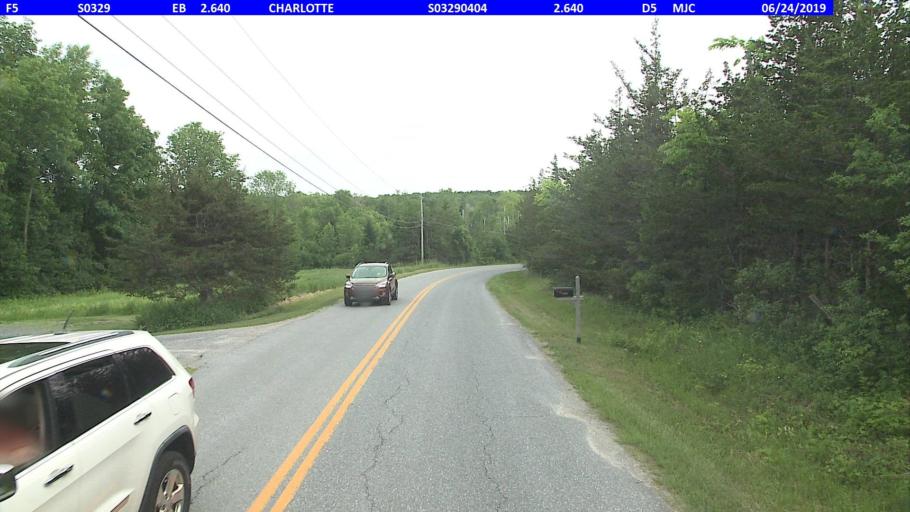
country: US
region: Vermont
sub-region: Addison County
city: Vergennes
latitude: 44.3033
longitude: -73.2938
